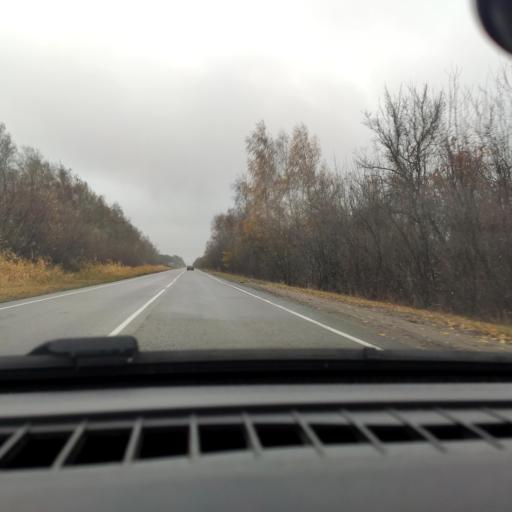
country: RU
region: Voronezj
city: Kolodeznyy
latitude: 51.3475
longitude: 39.0238
